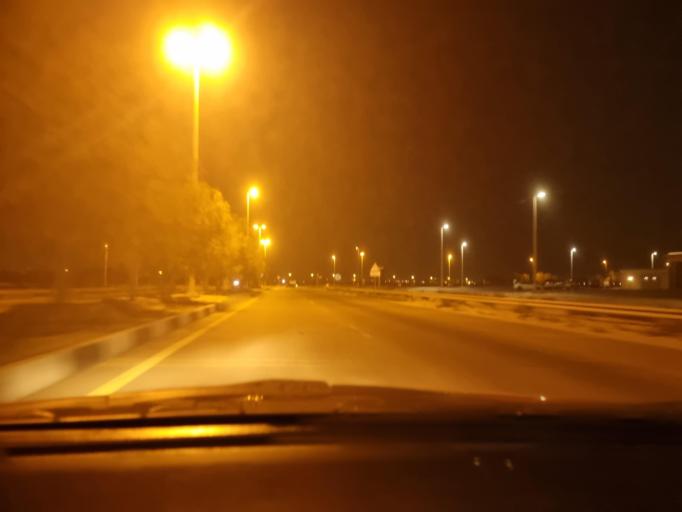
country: AE
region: Abu Dhabi
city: Abu Dhabi
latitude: 24.3855
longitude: 54.6812
